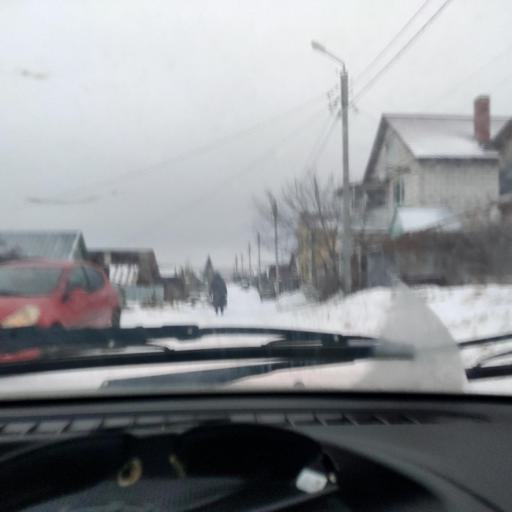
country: RU
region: Samara
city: Zhigulevsk
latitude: 53.4864
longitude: 49.5315
